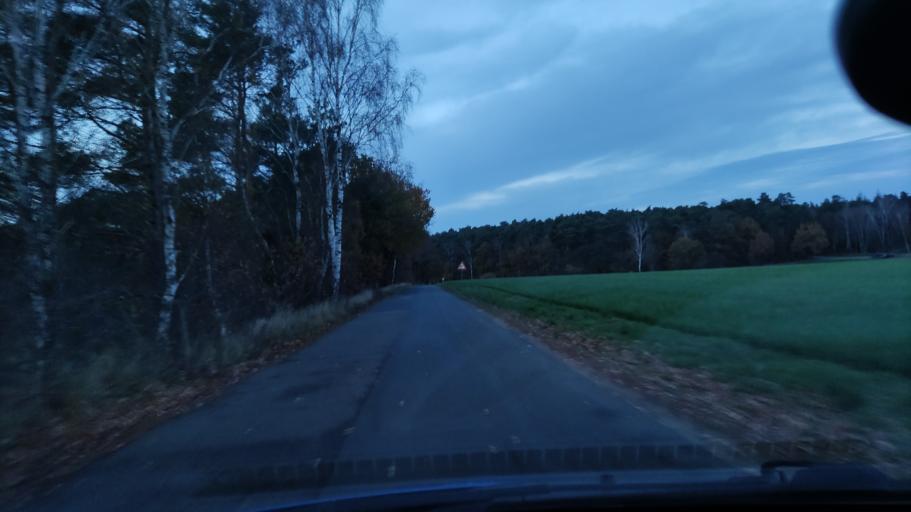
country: DE
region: Lower Saxony
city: Egestorf
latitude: 53.1508
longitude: 10.0320
